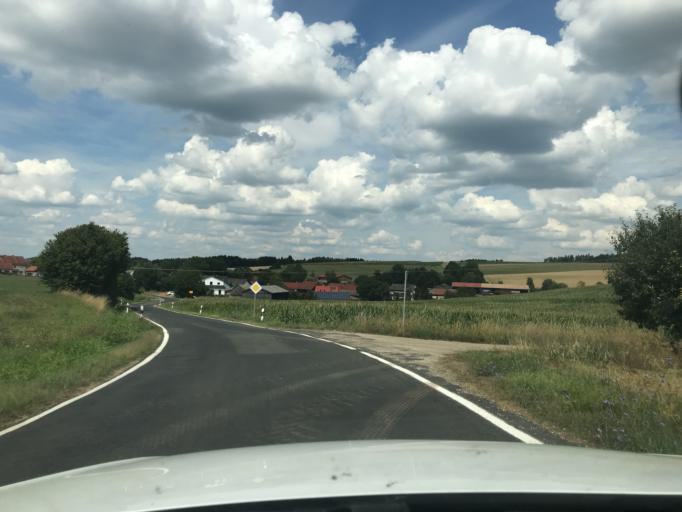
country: DE
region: Bavaria
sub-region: Upper Palatinate
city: Auerbach
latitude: 49.7387
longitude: 11.6382
